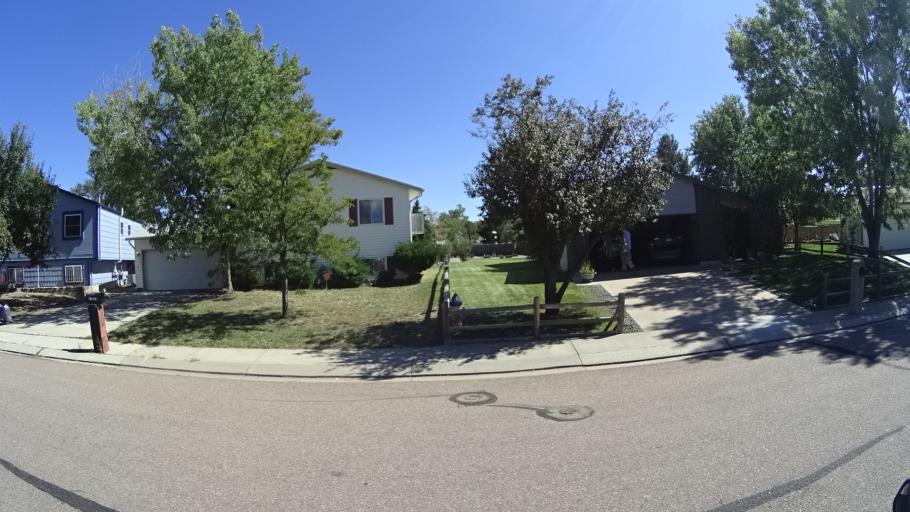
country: US
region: Colorado
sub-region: El Paso County
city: Stratmoor
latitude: 38.7872
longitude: -104.7480
